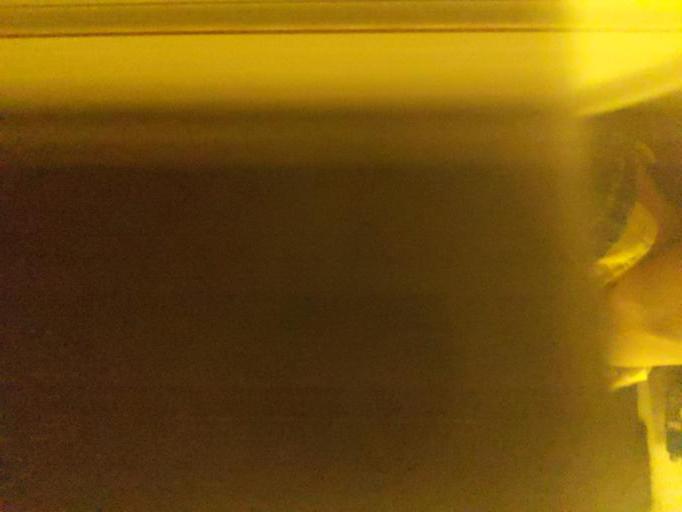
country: JP
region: Shizuoka
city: Shizuoka-shi
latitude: 35.0674
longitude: 138.5177
